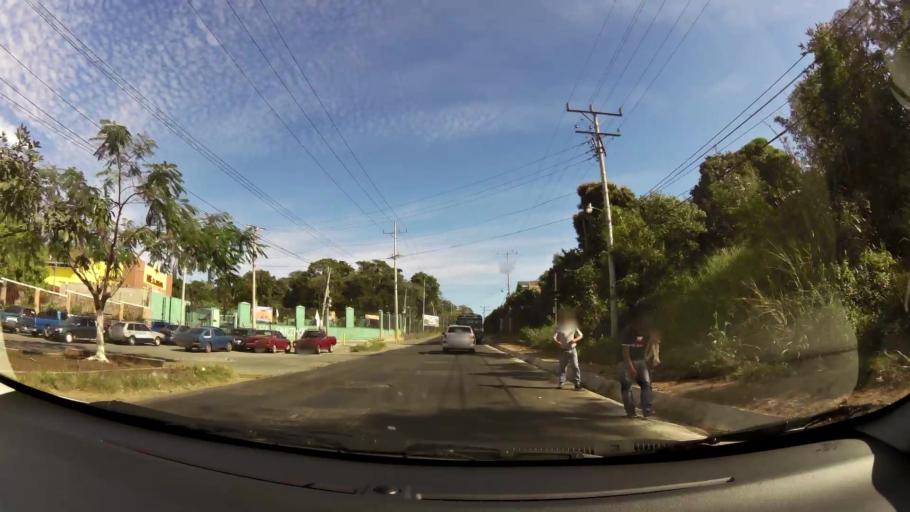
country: SV
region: Santa Ana
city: Santa Ana
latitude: 13.9843
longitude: -89.5868
